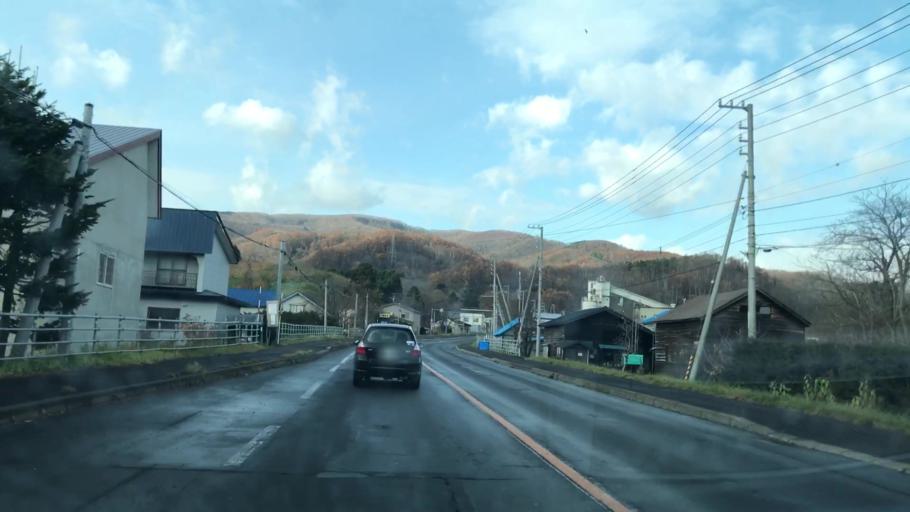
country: JP
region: Hokkaido
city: Yoichi
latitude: 43.2102
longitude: 140.7574
